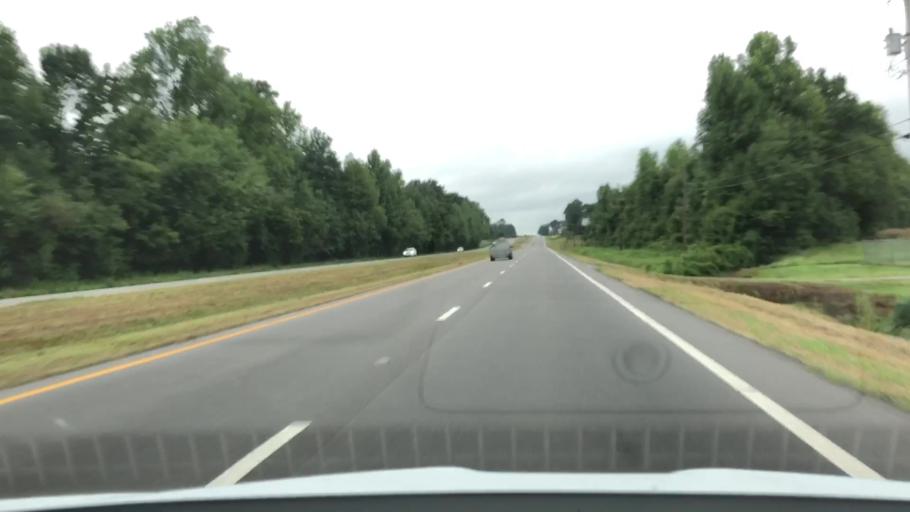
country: US
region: North Carolina
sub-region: Lenoir County
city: La Grange
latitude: 35.2728
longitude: -77.7427
